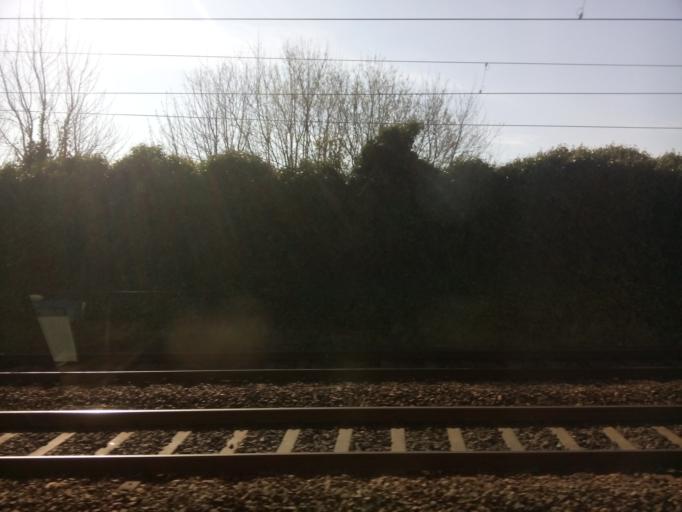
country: GB
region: Scotland
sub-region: Edinburgh
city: Colinton
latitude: 55.9334
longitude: -3.2723
